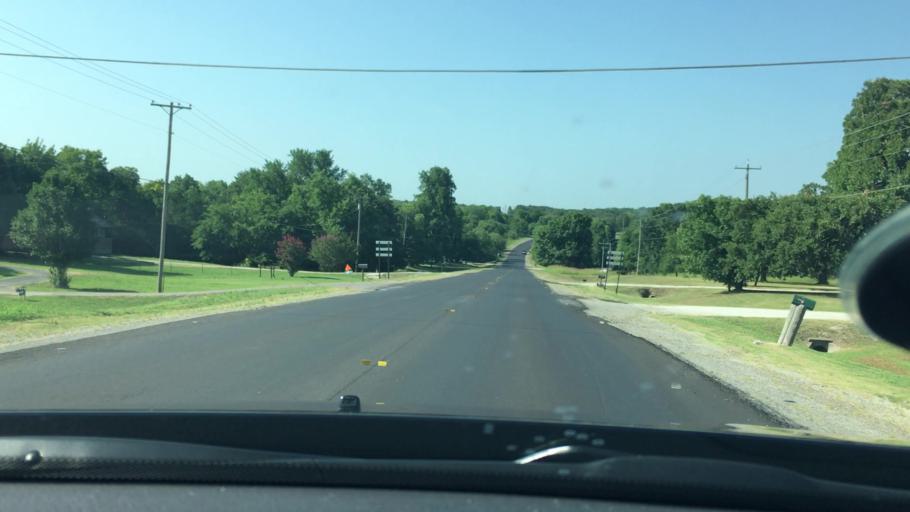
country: US
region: Oklahoma
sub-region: Pontotoc County
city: Ada
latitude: 34.7475
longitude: -96.6702
